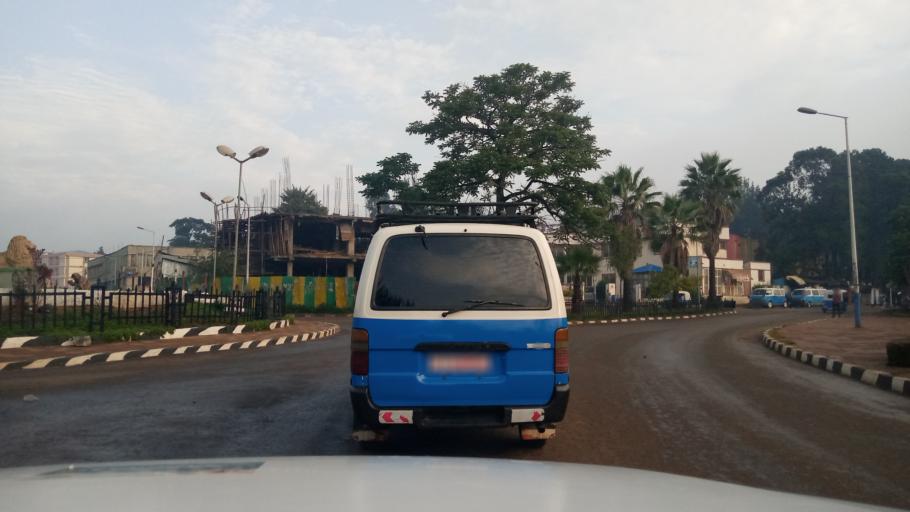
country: ET
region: Oromiya
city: Jima
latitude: 7.6762
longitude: 36.8346
